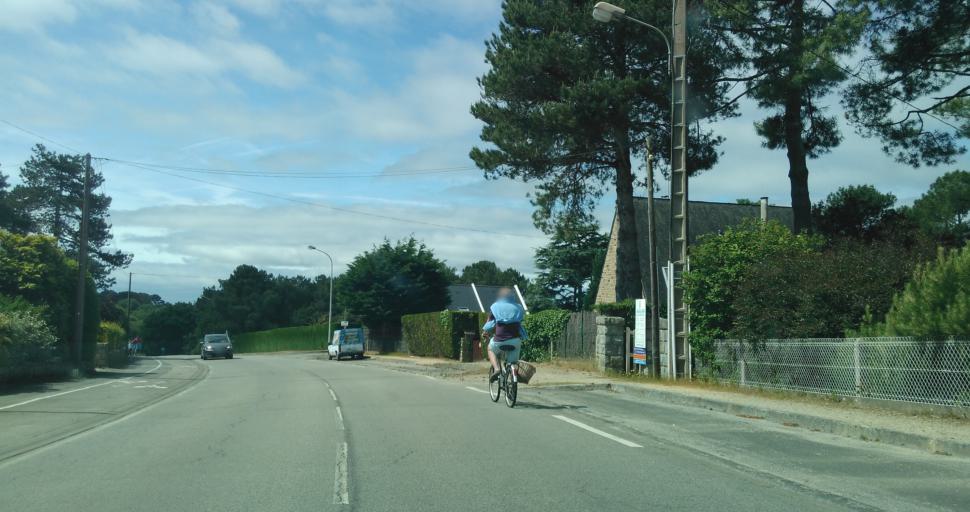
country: FR
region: Brittany
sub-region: Departement du Morbihan
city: La Trinite-sur-Mer
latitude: 47.5814
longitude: -3.0316
